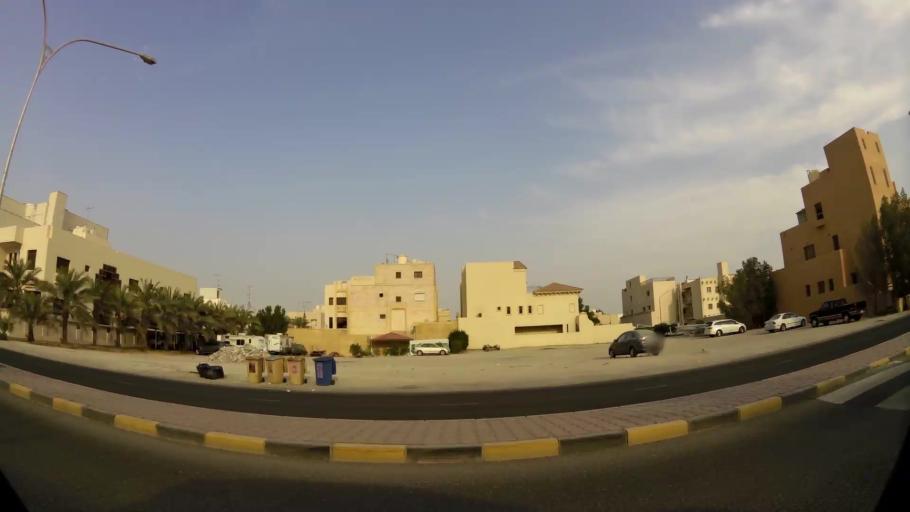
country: KW
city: Bayan
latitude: 29.3124
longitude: 48.0324
